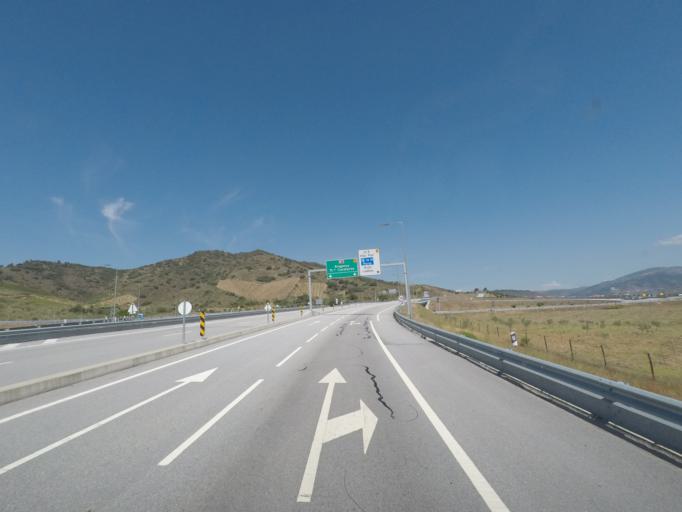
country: PT
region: Braganca
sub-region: Braganca Municipality
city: Vila Flor
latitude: 41.3227
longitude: -7.0794
